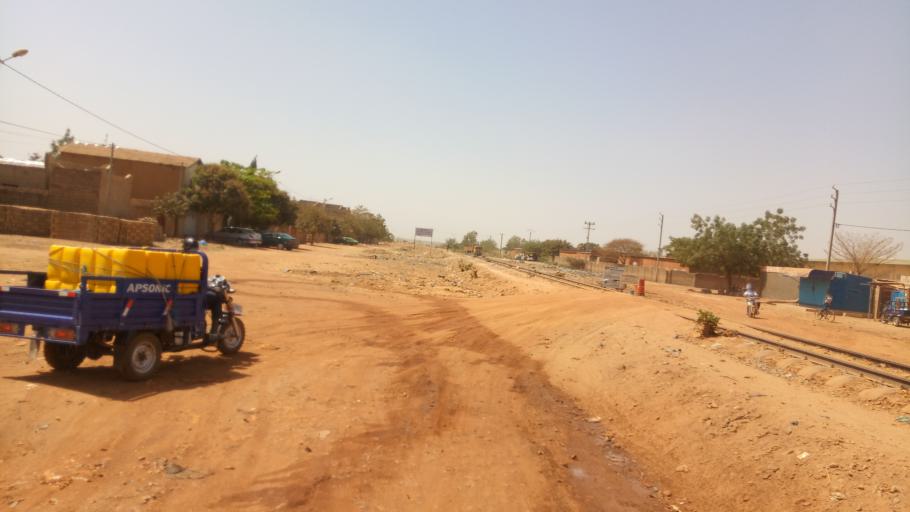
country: BF
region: Centre
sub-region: Kadiogo Province
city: Ouagadougou
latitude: 12.3844
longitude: -1.5671
